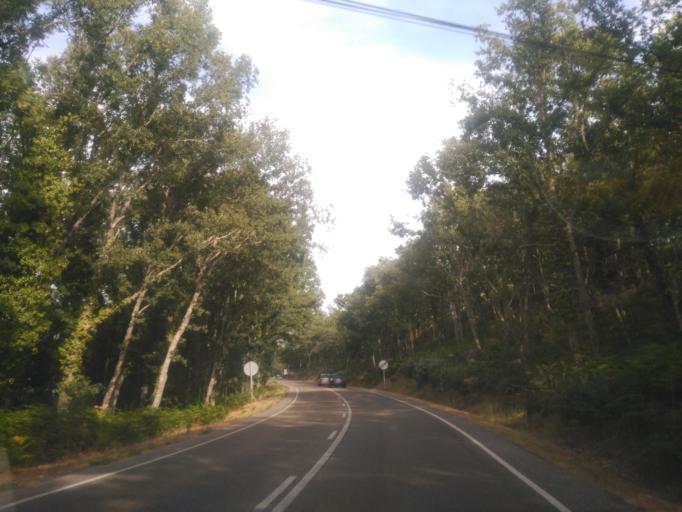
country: ES
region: Castille and Leon
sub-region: Provincia de Zamora
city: Galende
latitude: 42.1182
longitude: -6.6948
